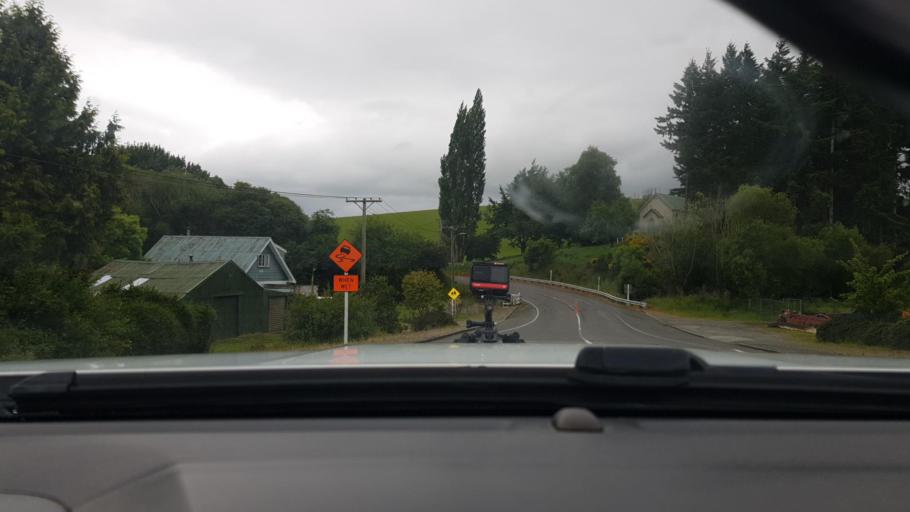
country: NZ
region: Southland
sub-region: Southland District
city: Winton
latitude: -45.8988
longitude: 168.3669
